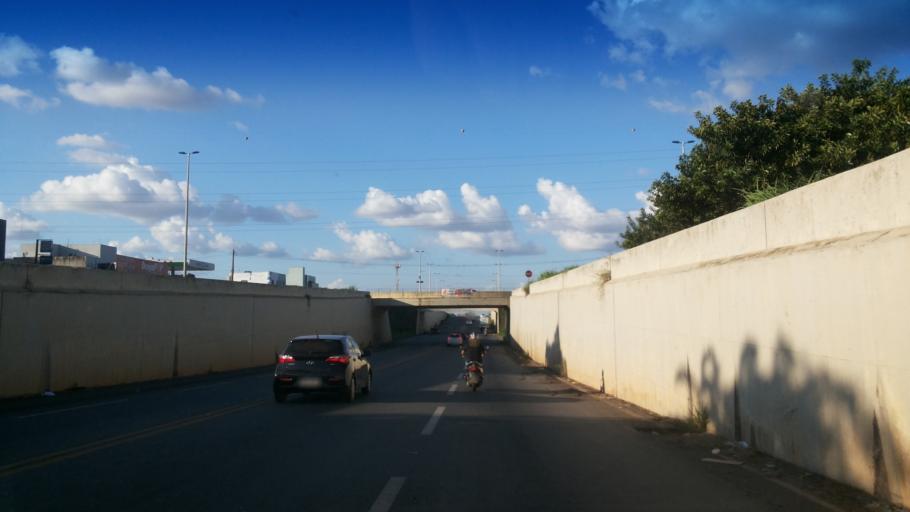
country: BR
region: Goias
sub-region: Goiania
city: Goiania
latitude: -16.7549
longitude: -49.3384
